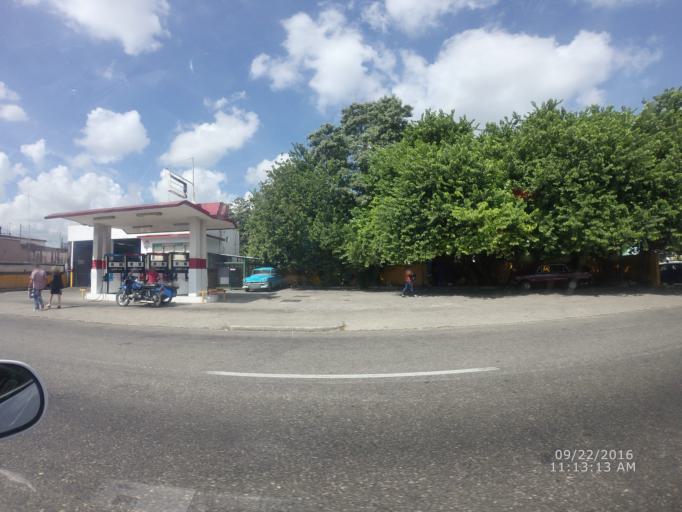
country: CU
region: La Habana
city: Cerro
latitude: 23.0906
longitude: -82.4215
